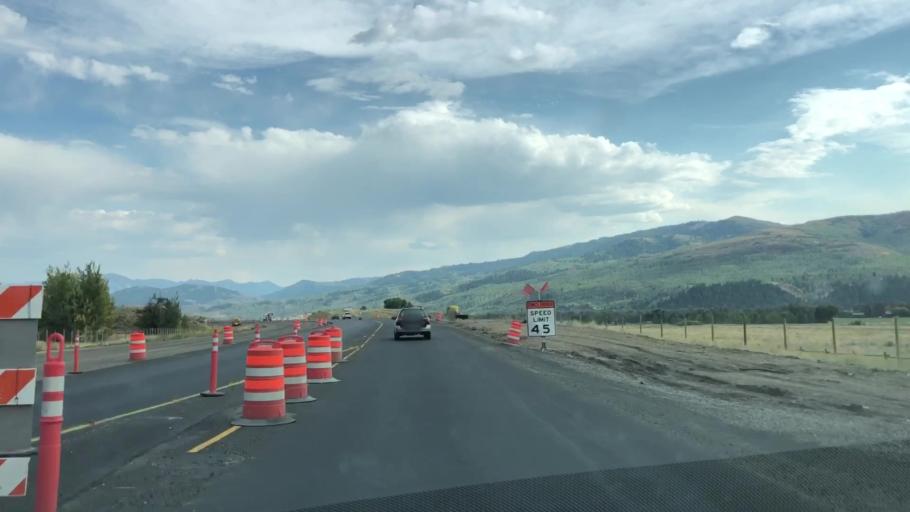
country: US
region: Wyoming
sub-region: Teton County
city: South Park
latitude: 43.4145
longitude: -110.7731
